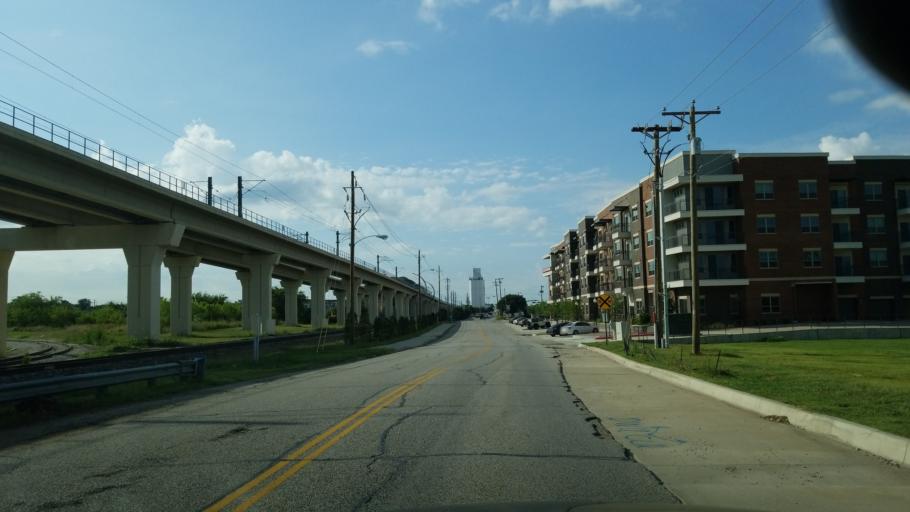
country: US
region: Texas
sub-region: Dallas County
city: Carrollton
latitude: 32.9565
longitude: -96.9101
